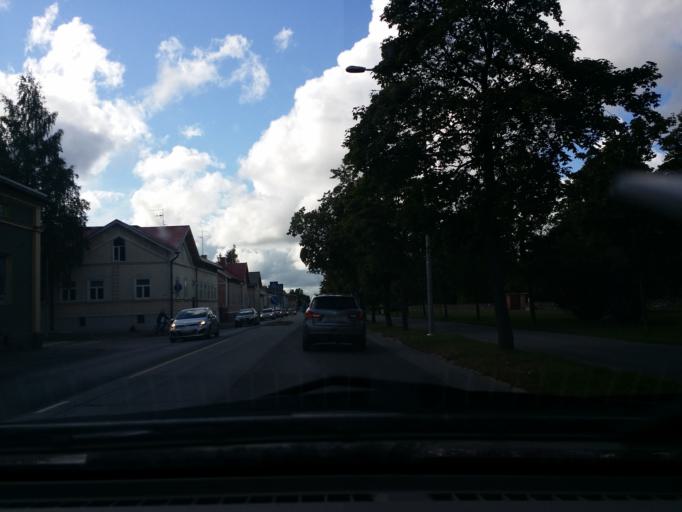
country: FI
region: Satakunta
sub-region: Pori
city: Pori
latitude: 61.4844
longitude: 21.7781
